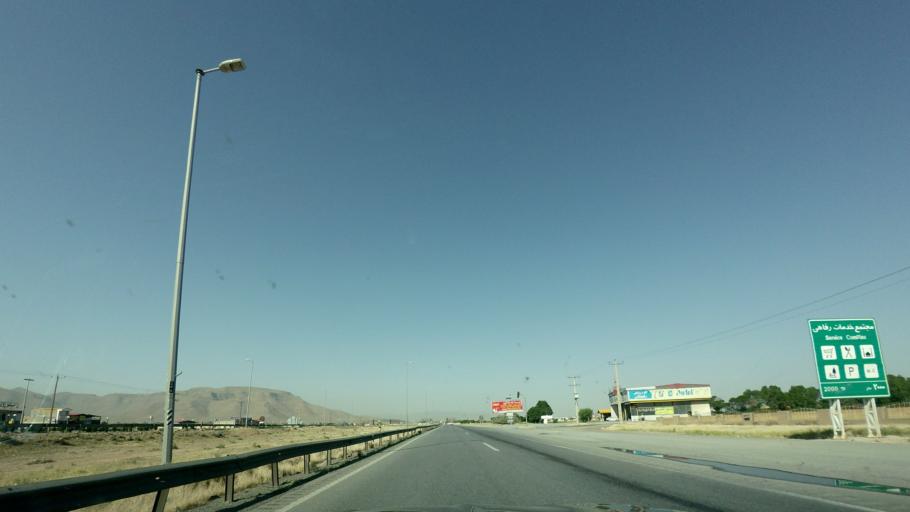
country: IR
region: Markazi
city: Arak
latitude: 34.1528
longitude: 49.9965
